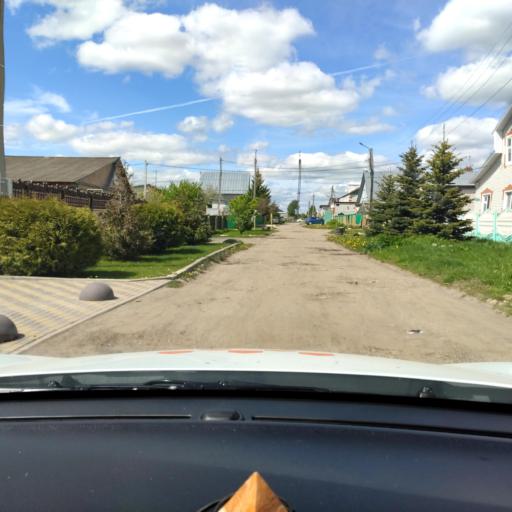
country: RU
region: Tatarstan
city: Osinovo
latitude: 55.8809
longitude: 48.8677
